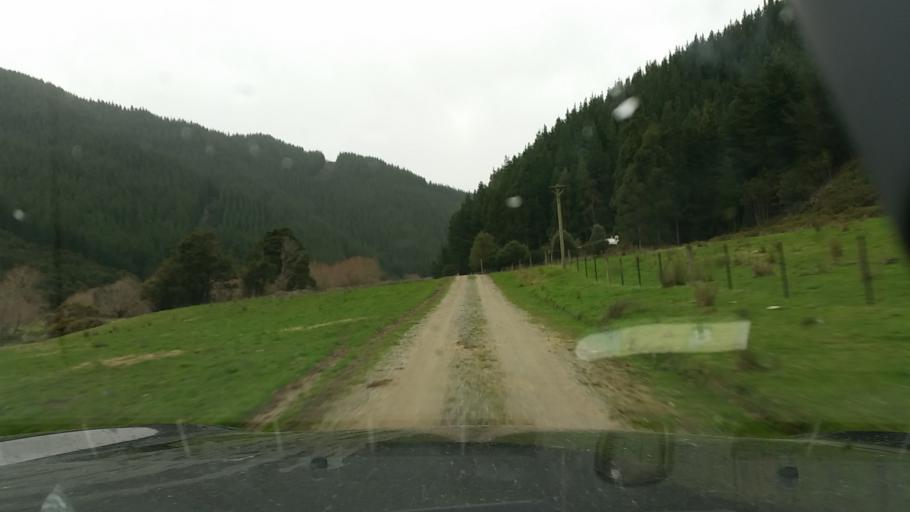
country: NZ
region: Marlborough
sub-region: Marlborough District
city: Blenheim
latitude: -41.3908
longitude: 173.8492
